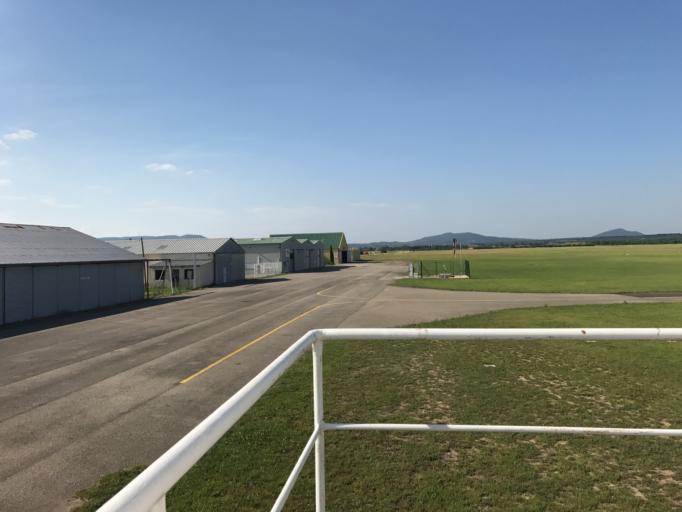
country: FR
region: Rhone-Alpes
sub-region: Departement de la Drome
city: Pierrelatte
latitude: 44.3907
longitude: 4.7120
